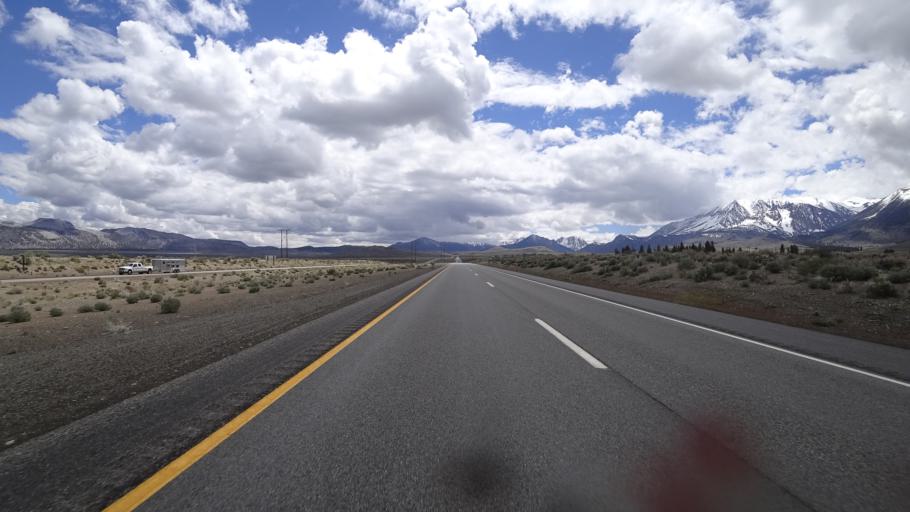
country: US
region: California
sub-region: Mono County
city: Mammoth Lakes
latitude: 37.8965
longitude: -119.0931
